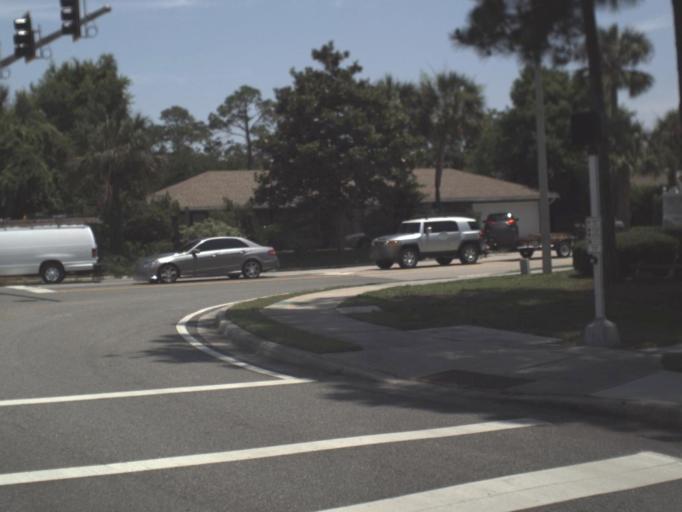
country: US
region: Florida
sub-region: Saint Johns County
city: Ponte Vedra Beach
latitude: 30.2271
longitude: -81.3852
